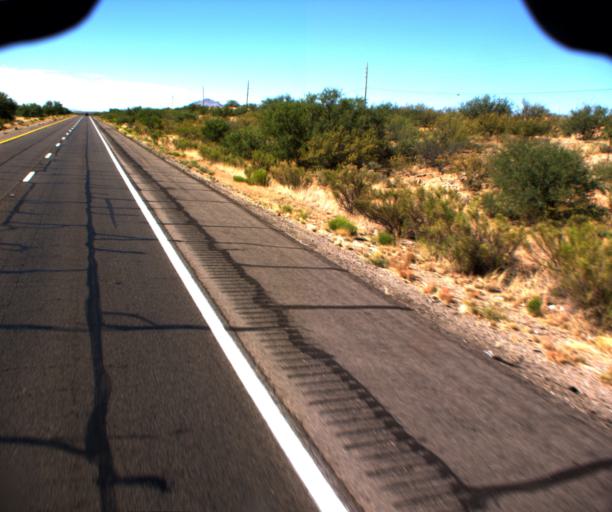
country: US
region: Arizona
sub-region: Pima County
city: Arivaca Junction
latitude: 31.6934
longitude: -111.0652
